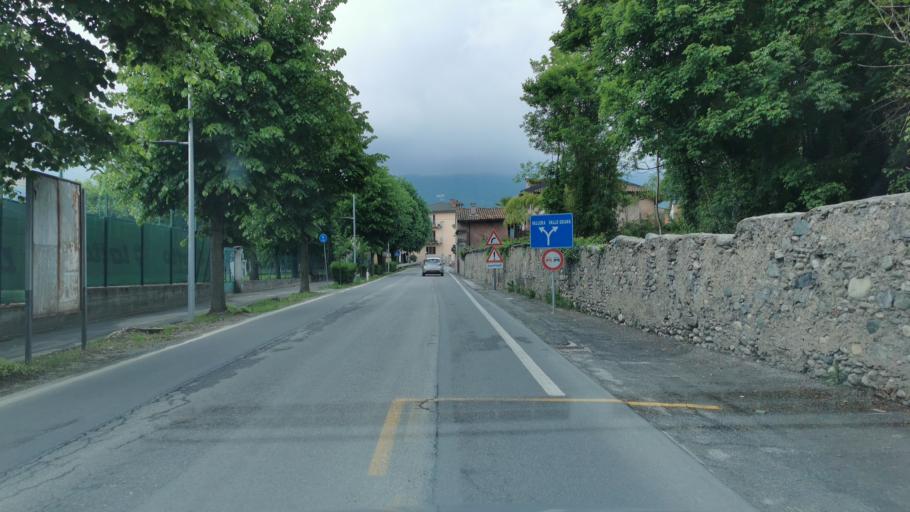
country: IT
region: Piedmont
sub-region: Provincia di Cuneo
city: Caraglio
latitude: 44.4145
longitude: 7.4235
